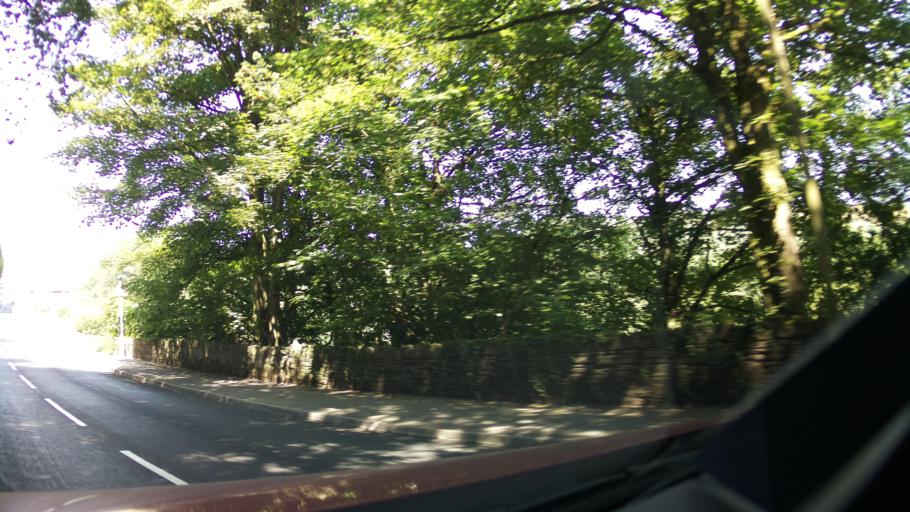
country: GB
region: Wales
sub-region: Caerphilly County Borough
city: Llanbradach
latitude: 51.5980
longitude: -3.2324
